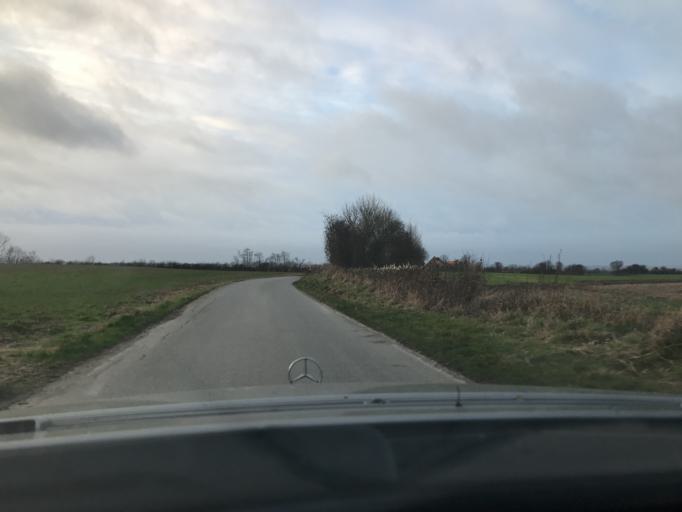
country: DK
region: South Denmark
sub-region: Sonderborg Kommune
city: Nordborg
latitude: 55.0528
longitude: 9.6837
